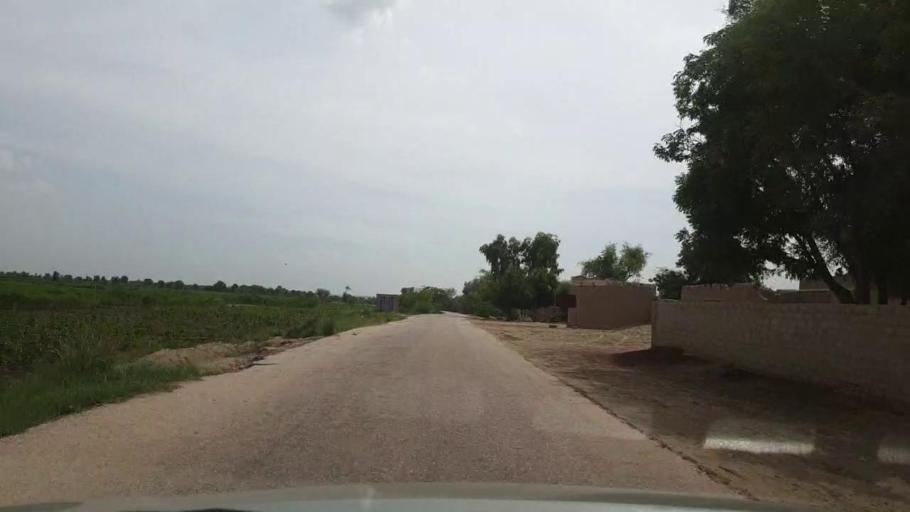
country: PK
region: Sindh
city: Kot Diji
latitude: 27.1477
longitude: 69.0303
